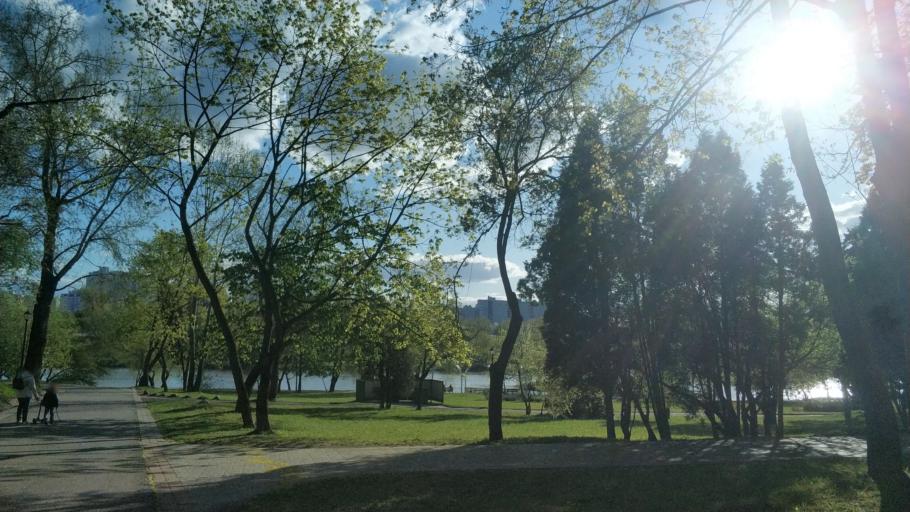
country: BY
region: Minsk
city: Syenitsa
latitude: 53.8518
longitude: 27.5772
